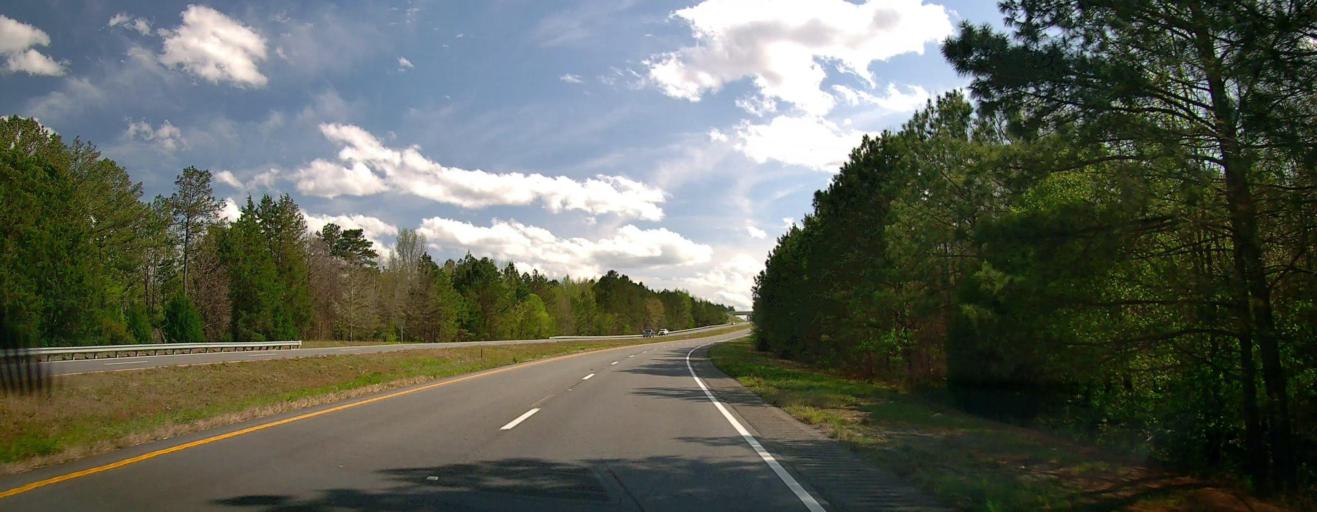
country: US
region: Georgia
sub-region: Baldwin County
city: Hardwick
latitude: 32.9855
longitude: -83.2123
